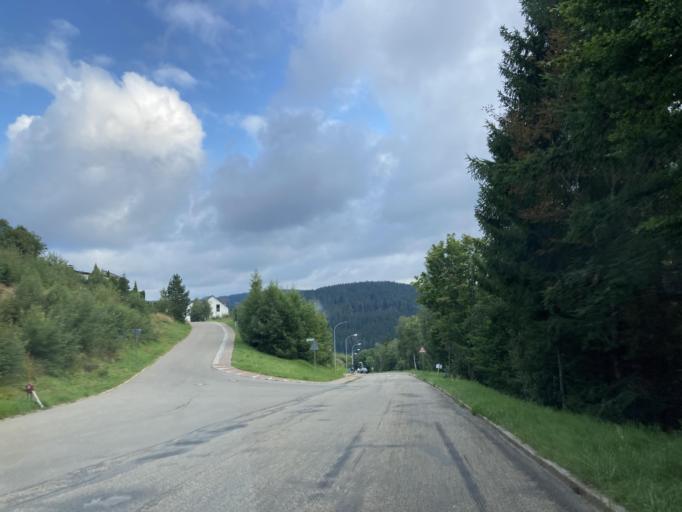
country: DE
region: Baden-Wuerttemberg
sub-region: Freiburg Region
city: Furtwangen im Schwarzwald
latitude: 48.0549
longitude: 8.1933
